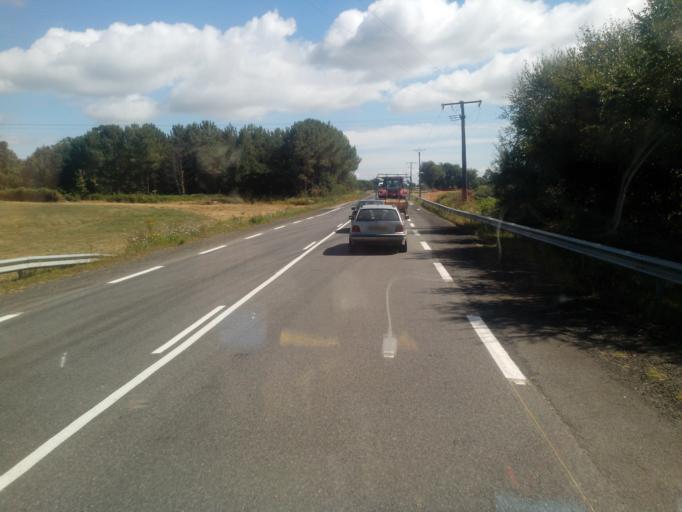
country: FR
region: Brittany
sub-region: Departement du Morbihan
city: Peaule
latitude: 47.6087
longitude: -2.3873
